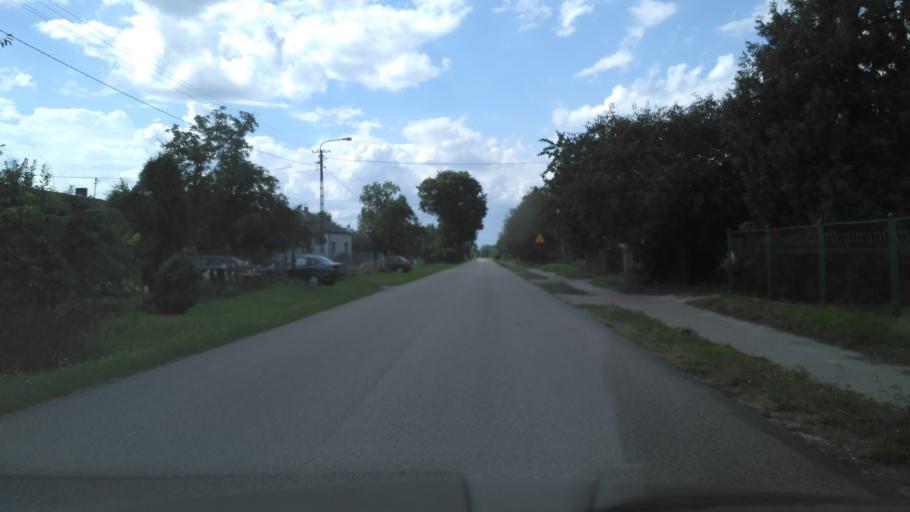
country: PL
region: Lublin Voivodeship
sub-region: Powiat swidnicki
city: Trawniki
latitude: 51.1756
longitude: 22.9704
